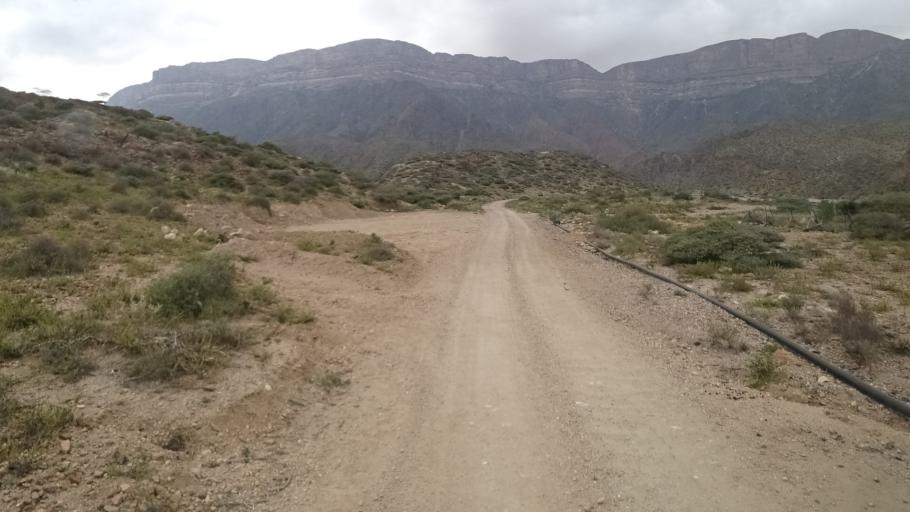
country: OM
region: Zufar
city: Salalah
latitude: 17.1720
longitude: 54.9521
